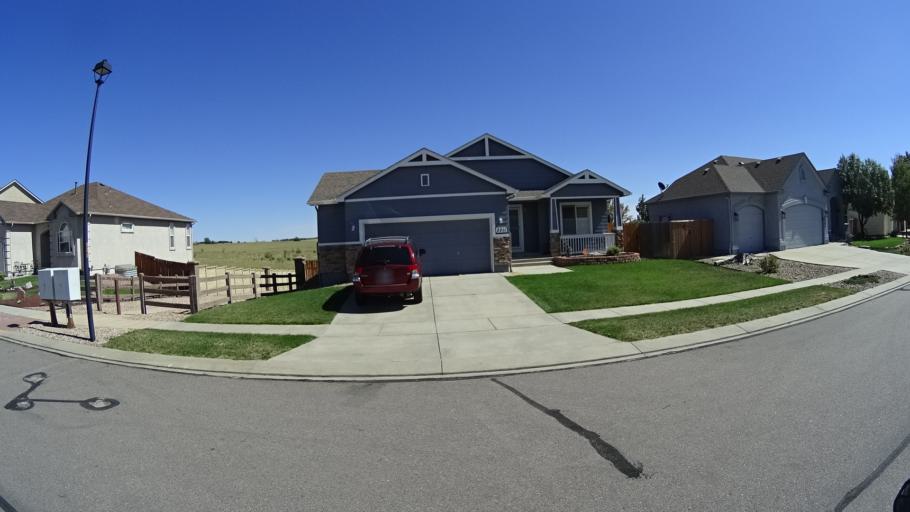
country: US
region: Colorado
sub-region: El Paso County
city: Security-Widefield
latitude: 38.7828
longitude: -104.7271
